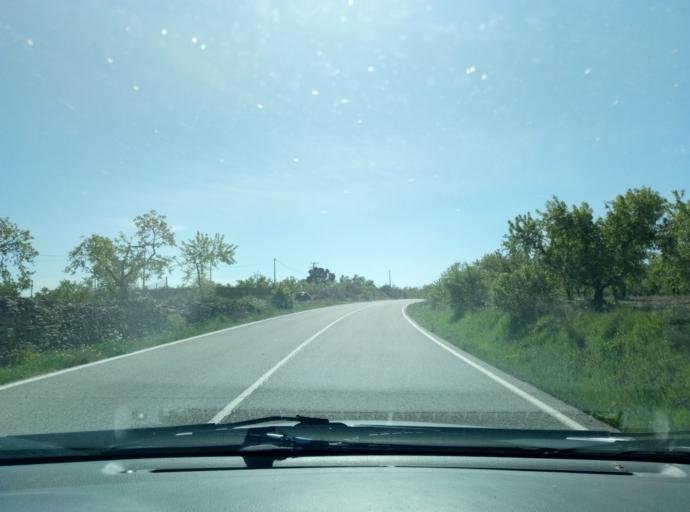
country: ES
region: Catalonia
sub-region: Provincia de Lleida
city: Vallbona de les Monges
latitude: 41.5454
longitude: 1.0280
